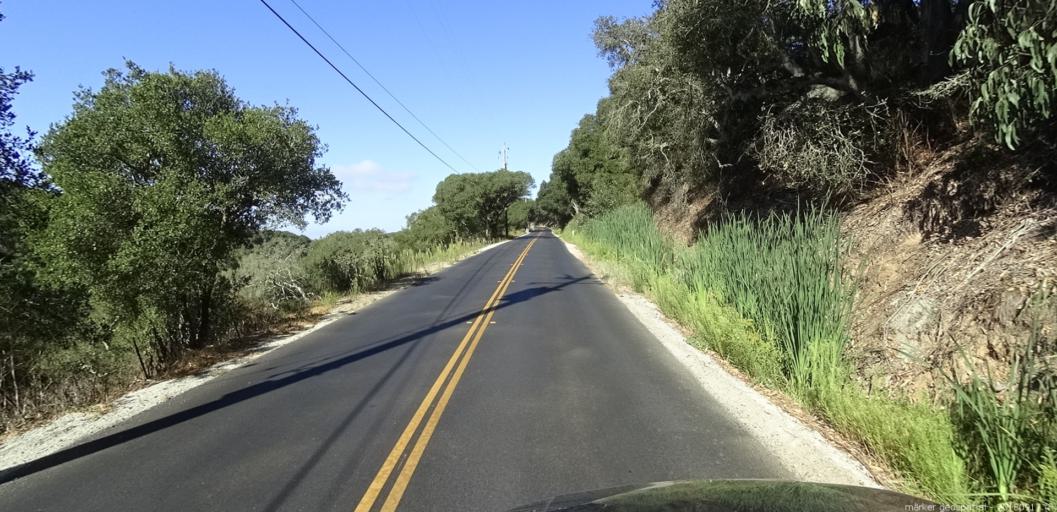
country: US
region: California
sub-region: Monterey County
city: Elkhorn
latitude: 36.8155
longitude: -121.7226
